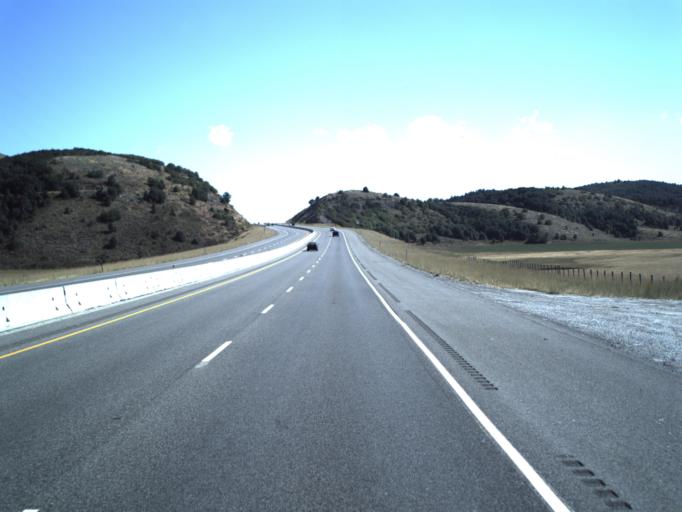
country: US
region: Utah
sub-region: Box Elder County
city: Brigham City
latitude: 41.5646
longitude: -111.9645
